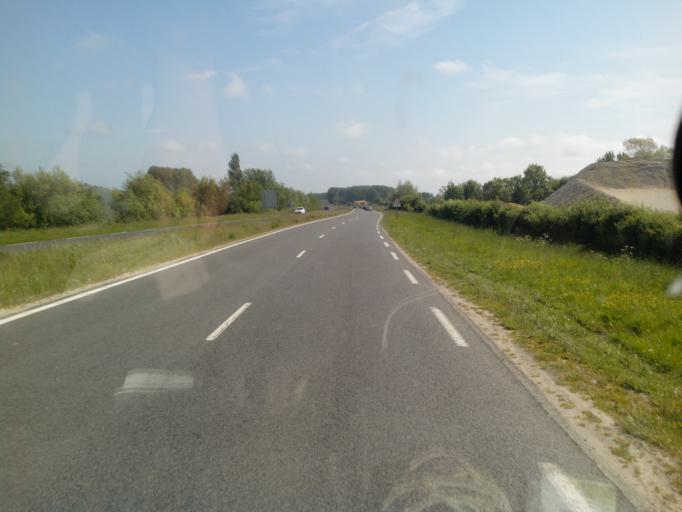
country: FR
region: Picardie
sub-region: Departement de la Somme
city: Quend
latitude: 50.2937
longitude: 1.6509
